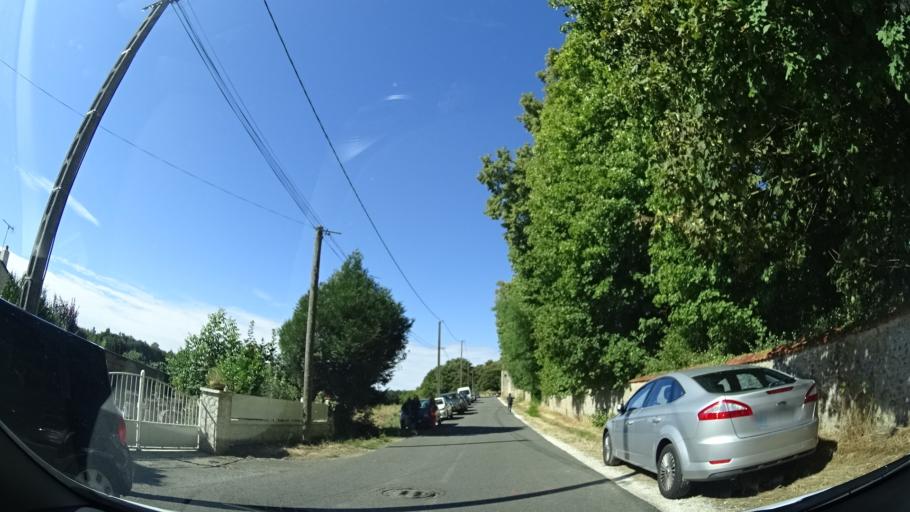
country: FR
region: Centre
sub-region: Departement du Loiret
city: Trigueres
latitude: 47.9406
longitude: 2.9873
